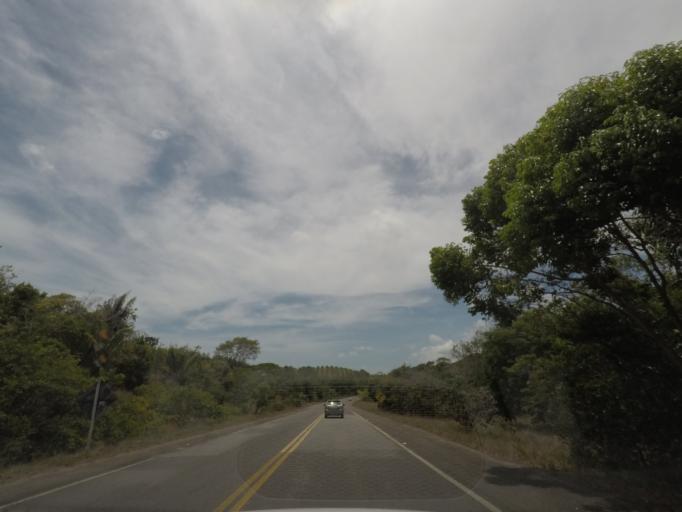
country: BR
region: Bahia
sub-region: Conde
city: Conde
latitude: -12.0286
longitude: -37.6975
